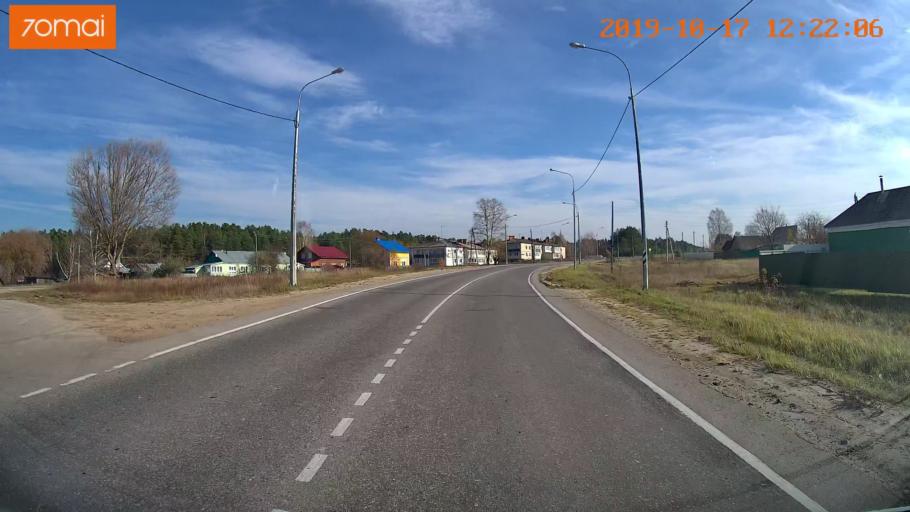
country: RU
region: Rjazan
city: Gus'-Zheleznyy
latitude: 55.0536
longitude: 41.1661
